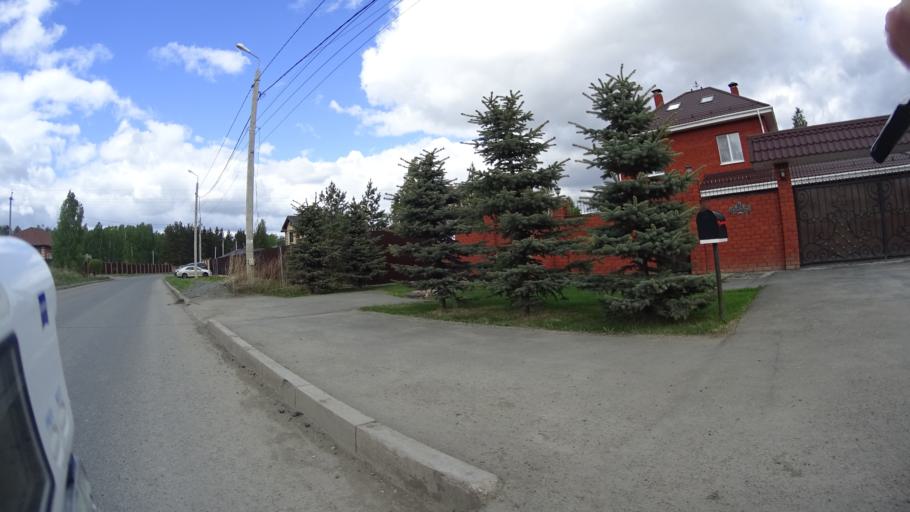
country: RU
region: Chelyabinsk
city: Sargazy
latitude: 55.1606
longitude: 61.2519
